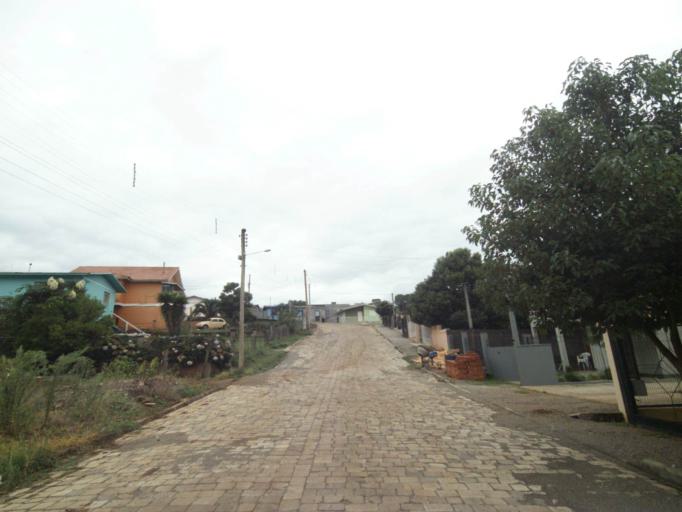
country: BR
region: Rio Grande do Sul
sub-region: Lagoa Vermelha
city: Lagoa Vermelha
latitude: -28.2135
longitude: -51.5279
